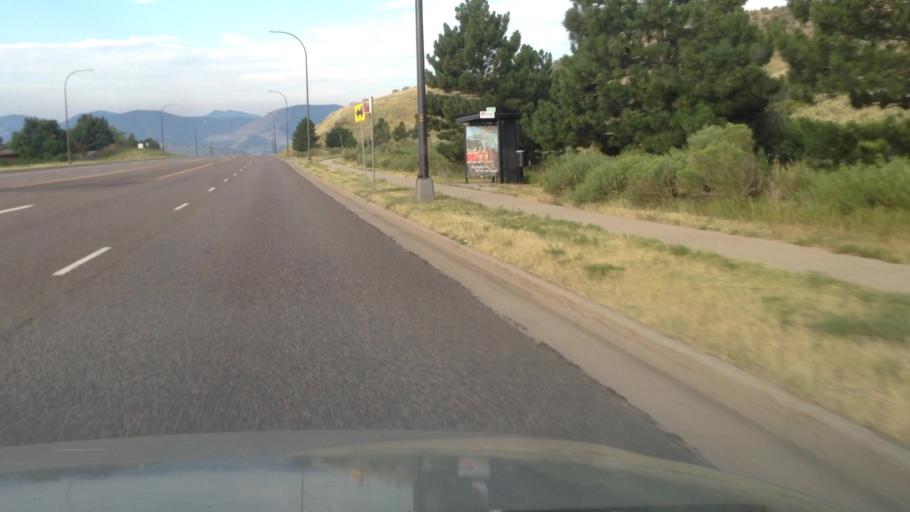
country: US
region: Colorado
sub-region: Jefferson County
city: West Pleasant View
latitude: 39.6905
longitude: -105.1513
